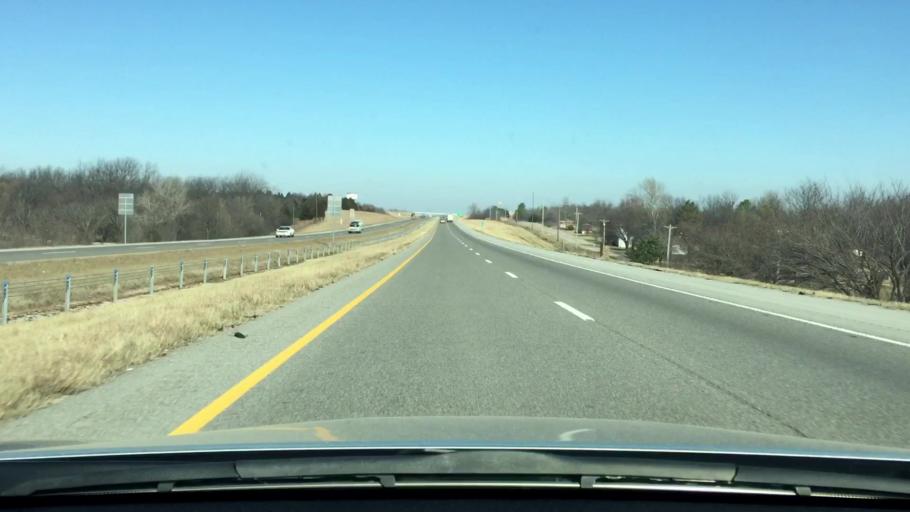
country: US
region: Oklahoma
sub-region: McClain County
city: Purcell
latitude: 34.9695
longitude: -97.3706
